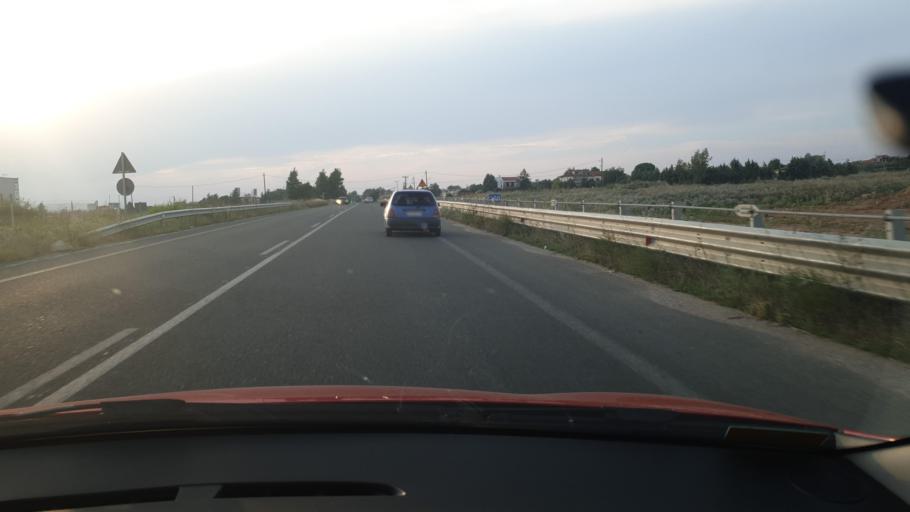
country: GR
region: Central Macedonia
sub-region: Nomos Thessalonikis
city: Agia Paraskevi
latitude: 40.5192
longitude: 23.0619
